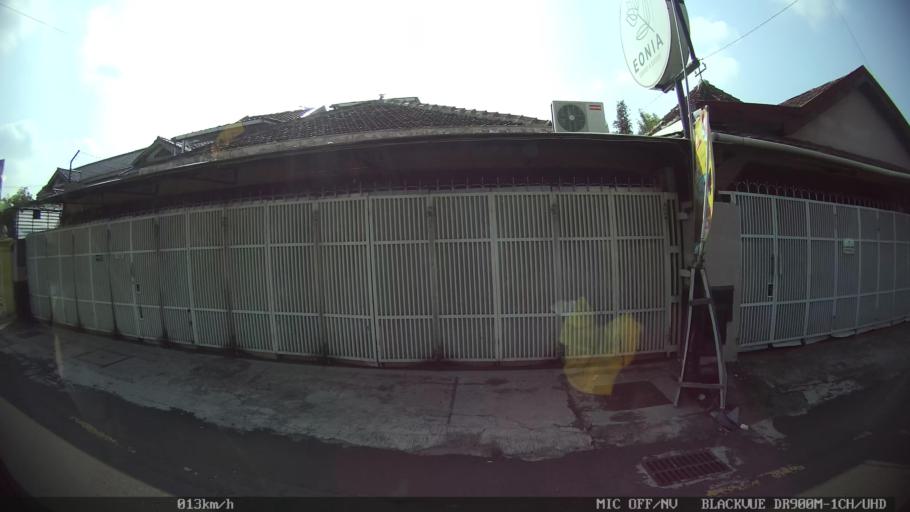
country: ID
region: Daerah Istimewa Yogyakarta
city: Yogyakarta
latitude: -7.8132
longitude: 110.3717
